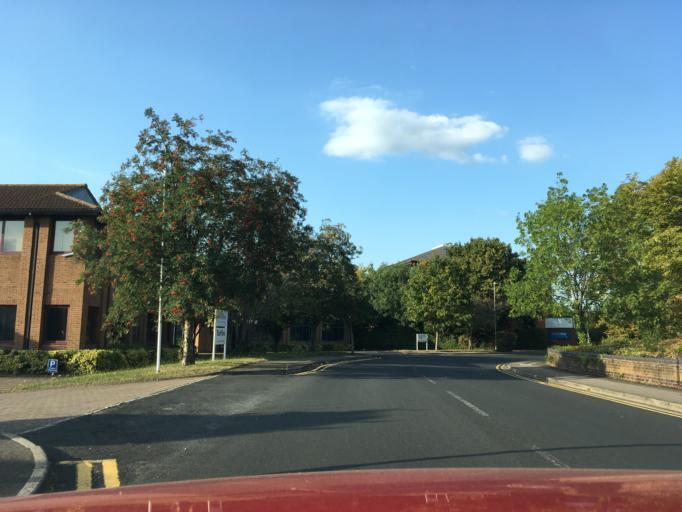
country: GB
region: England
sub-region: Gloucestershire
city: Barnwood
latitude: 51.8651
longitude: -2.2053
